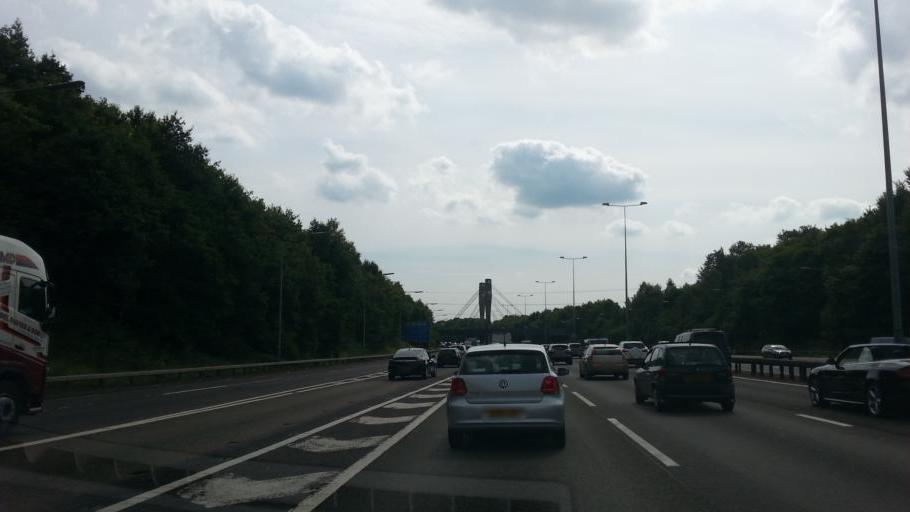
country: GB
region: England
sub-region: Surrey
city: Chertsey
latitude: 51.3958
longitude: -0.5343
